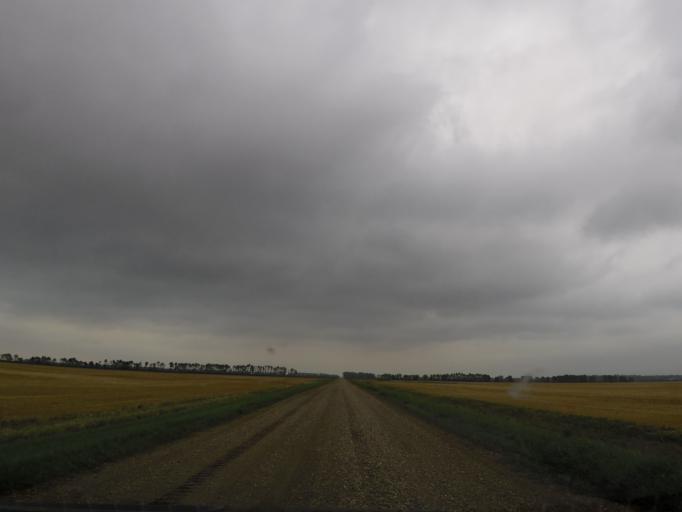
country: US
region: North Dakota
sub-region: Walsh County
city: Grafton
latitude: 48.4866
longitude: -97.1688
